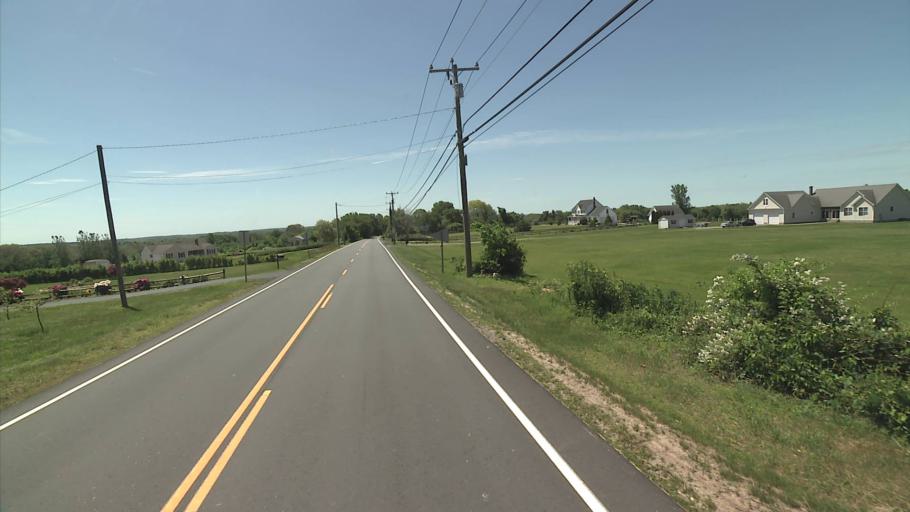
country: US
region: Connecticut
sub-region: Windham County
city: Plainfield
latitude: 41.6424
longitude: -71.8469
